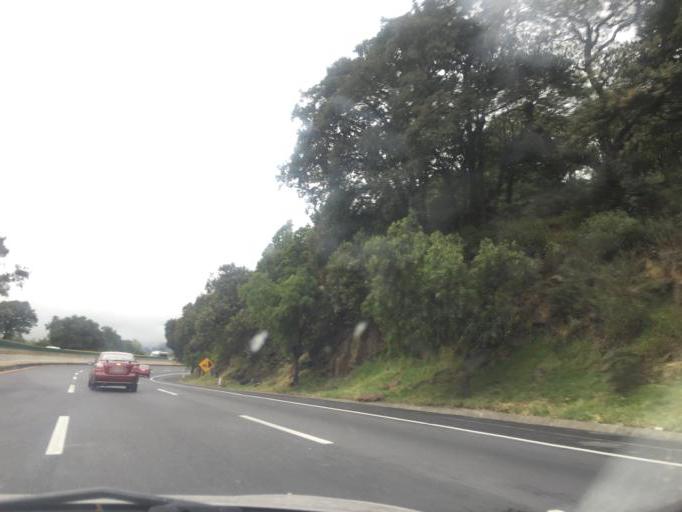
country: MX
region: Mexico City
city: Xochimilco
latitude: 19.2190
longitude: -99.1309
